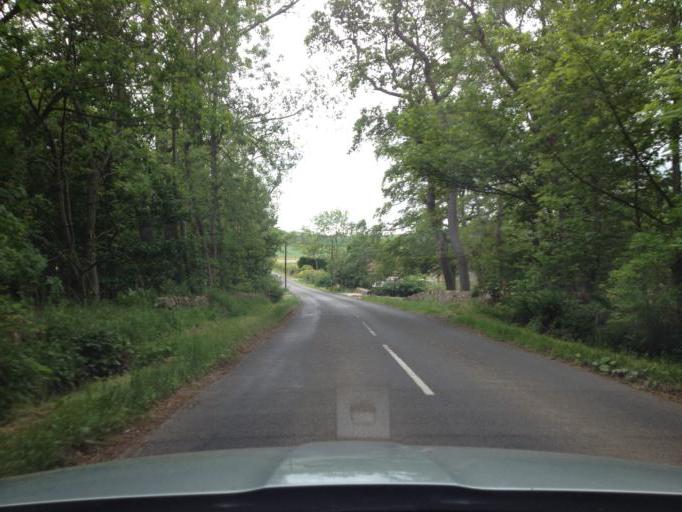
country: GB
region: Scotland
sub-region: Fife
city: Strathkinness
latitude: 56.3232
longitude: -2.8742
